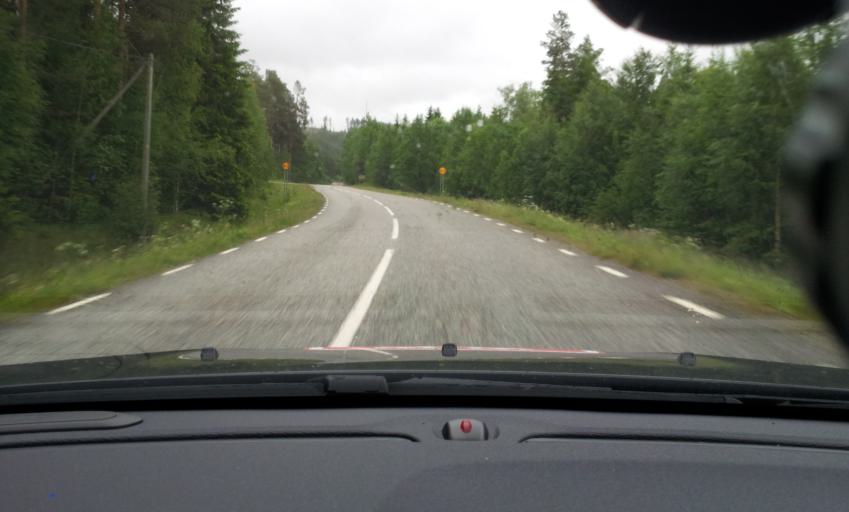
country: SE
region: Jaemtland
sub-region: Stroemsunds Kommun
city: Stroemsund
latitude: 63.3418
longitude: 15.7573
